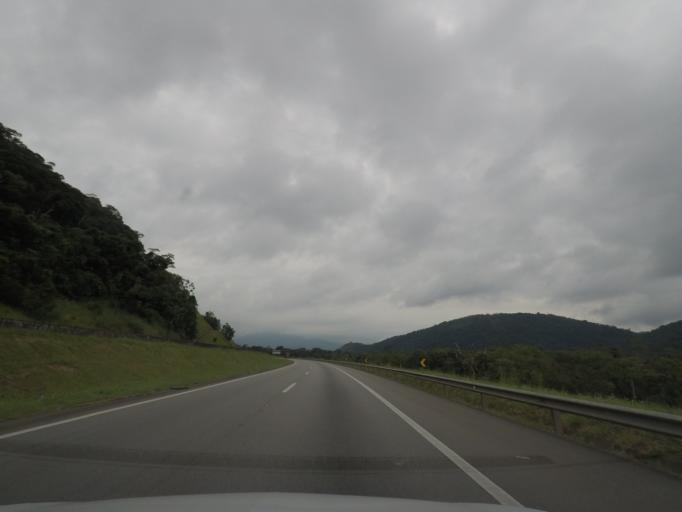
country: BR
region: Sao Paulo
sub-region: Miracatu
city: Miracatu
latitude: -24.2046
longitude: -47.3723
